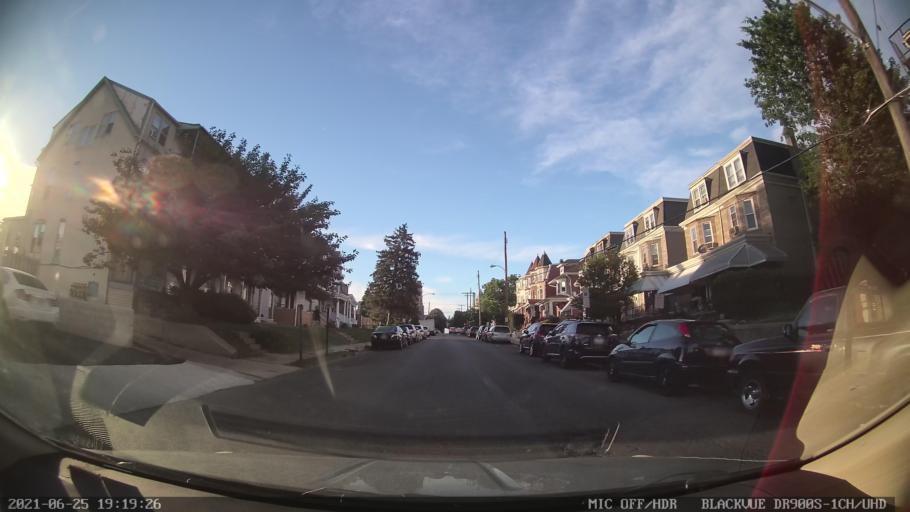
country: US
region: Pennsylvania
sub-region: Berks County
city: Reading
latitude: 40.3479
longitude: -75.9353
